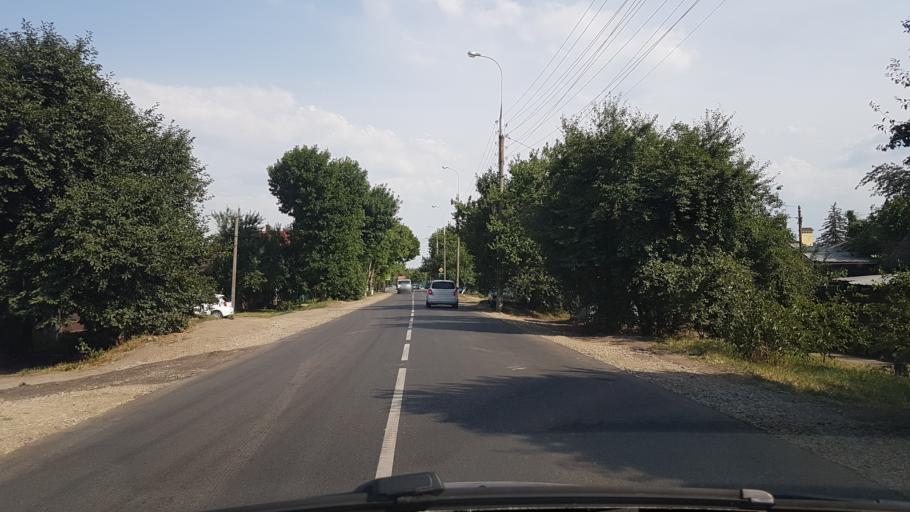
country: RU
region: Krasnodarskiy
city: Pashkovskiy
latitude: 45.0284
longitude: 39.1244
